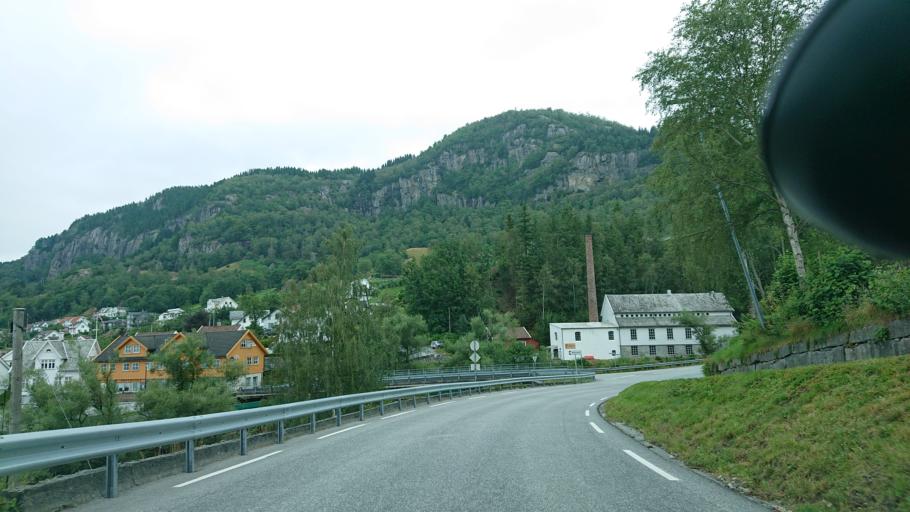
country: NO
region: Rogaland
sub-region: Hjelmeland
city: Hjelmelandsvagen
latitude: 59.2359
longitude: 6.1797
